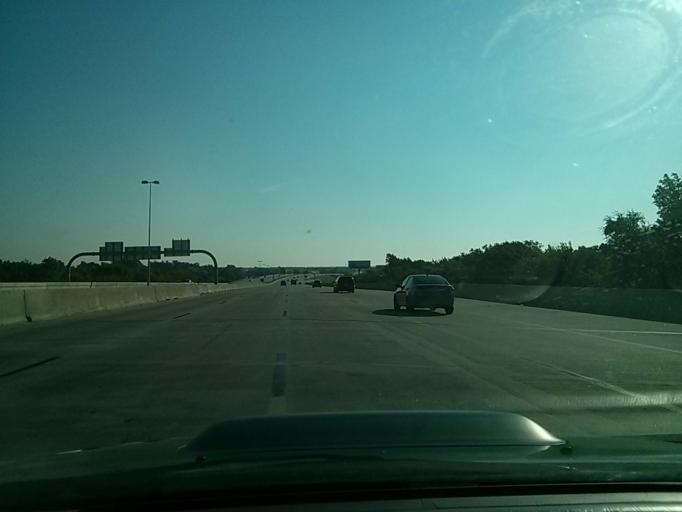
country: US
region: Oklahoma
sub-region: Tulsa County
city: Owasso
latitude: 36.1624
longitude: -95.8781
